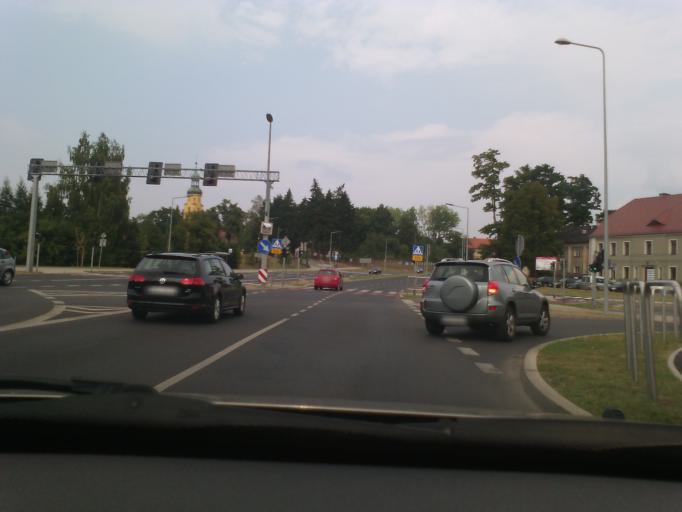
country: PL
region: Lower Silesian Voivodeship
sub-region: Powiat walbrzyski
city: Szczawno-Zdroj
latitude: 50.8251
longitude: 16.2893
